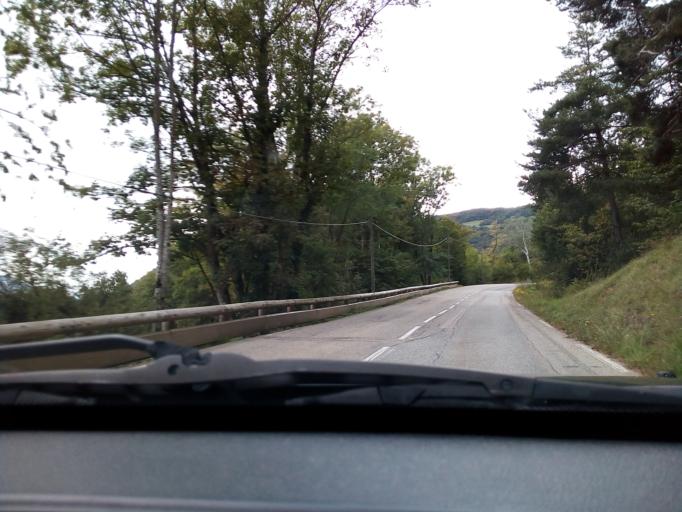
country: FR
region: Rhone-Alpes
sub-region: Departement de l'Isere
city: Corenc
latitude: 45.2250
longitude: 5.7627
